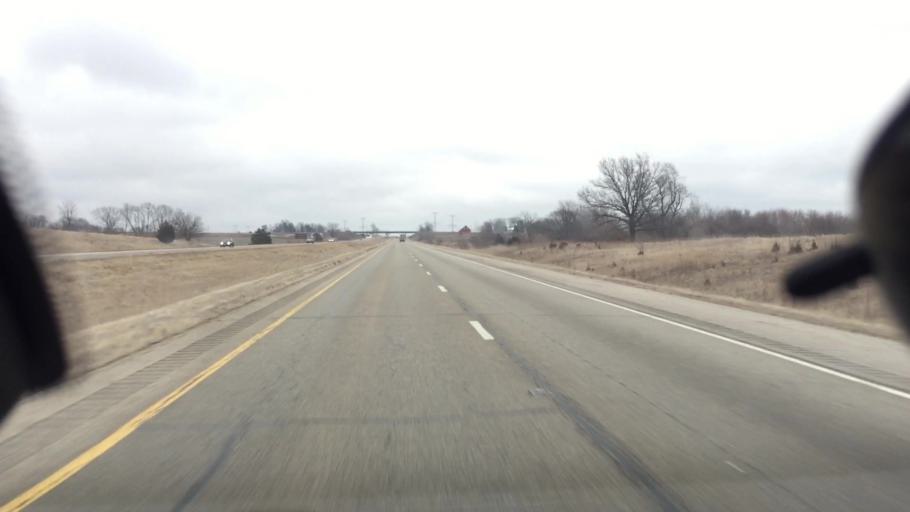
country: US
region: Illinois
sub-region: Tazewell County
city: Morton
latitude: 40.6215
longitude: -89.4149
